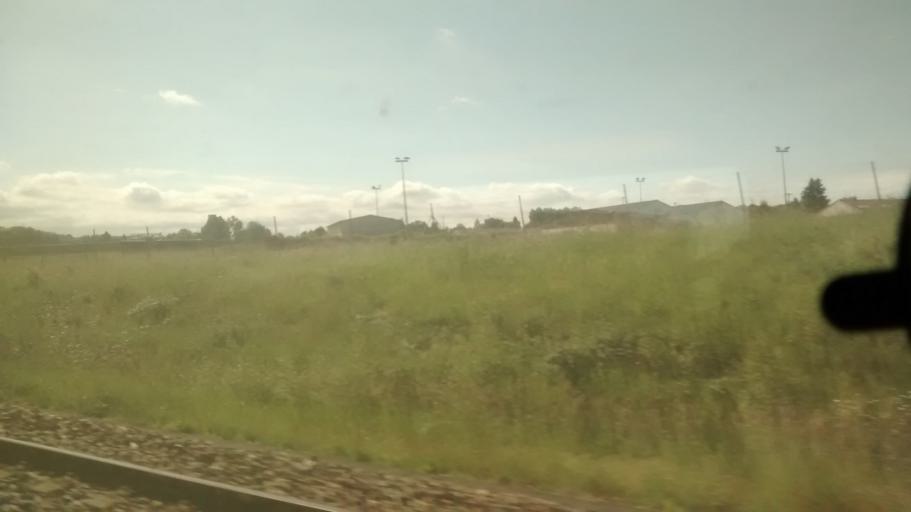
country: FR
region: Pays de la Loire
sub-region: Departement de la Sarthe
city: Thorigne-sur-Due
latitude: 48.0459
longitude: 0.5283
